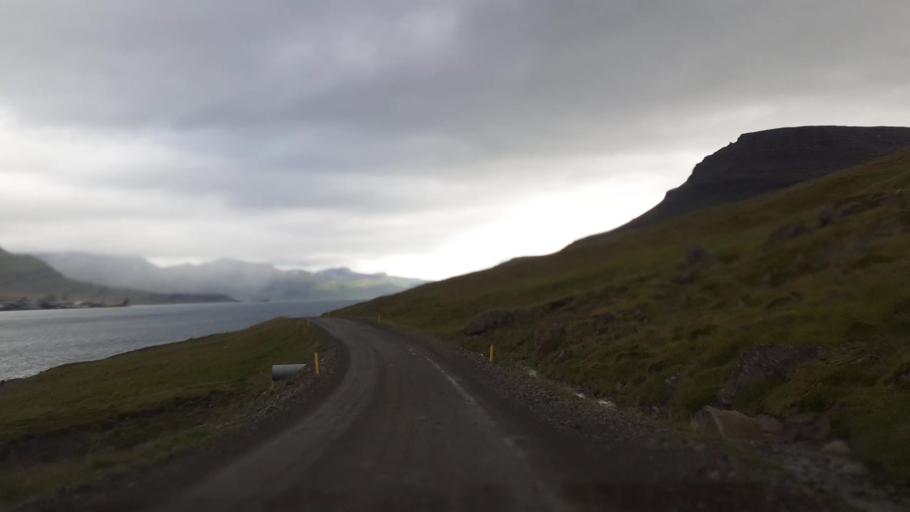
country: IS
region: East
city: Reydarfjoerdur
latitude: 65.0124
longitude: -14.1778
